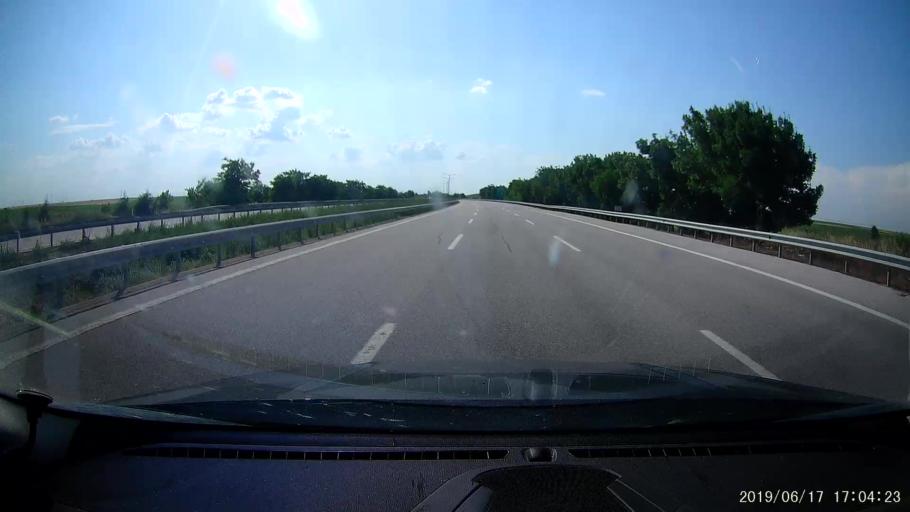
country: TR
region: Edirne
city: Haskoy
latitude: 41.6546
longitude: 26.7291
